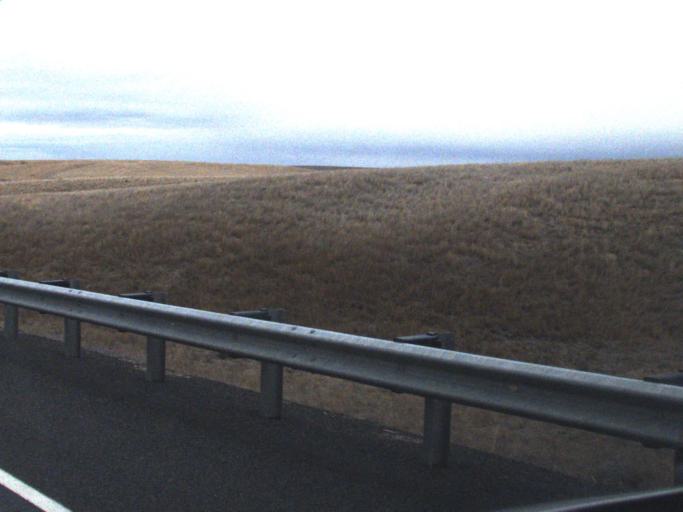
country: US
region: Washington
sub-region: Adams County
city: Ritzville
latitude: 46.7700
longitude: -118.3512
